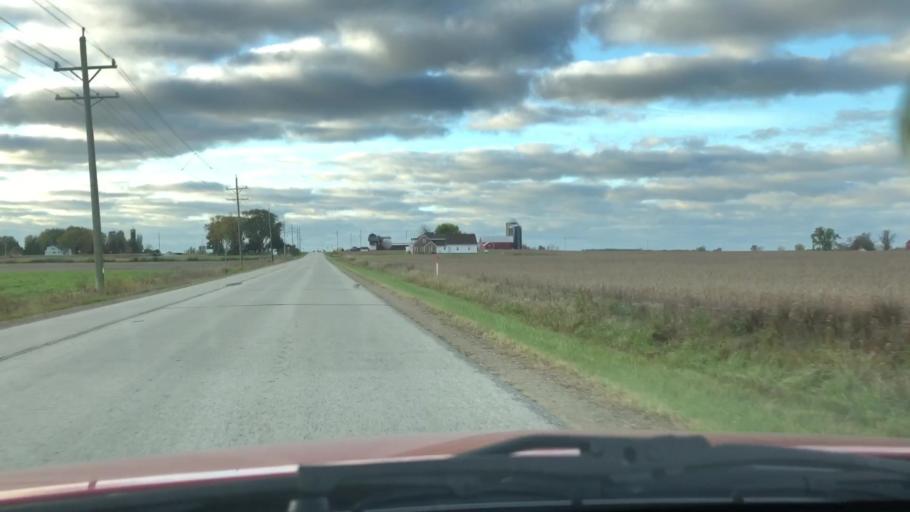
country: US
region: Wisconsin
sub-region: Outagamie County
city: Seymour
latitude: 44.5049
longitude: -88.3104
